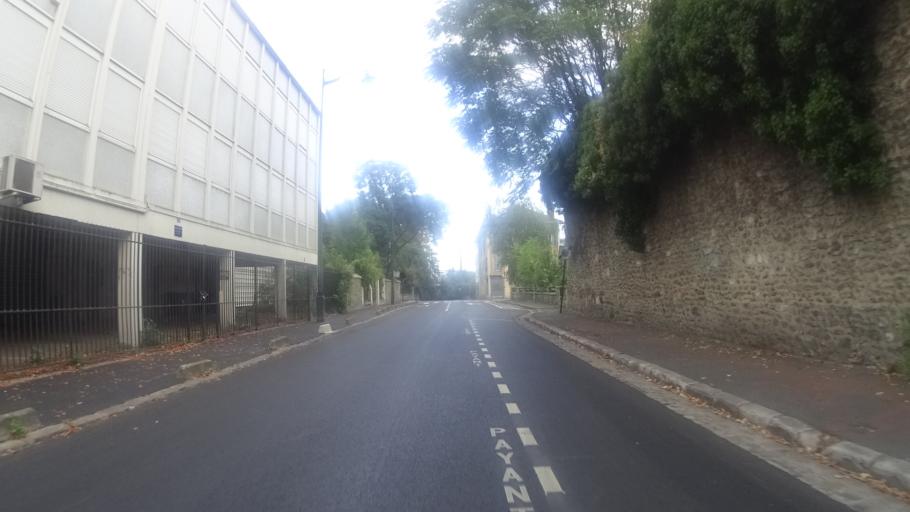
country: FR
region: Ile-de-France
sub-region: Departement de l'Essonne
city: Saint-Germain-les-Corbeil
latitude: 48.6151
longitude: 2.4758
